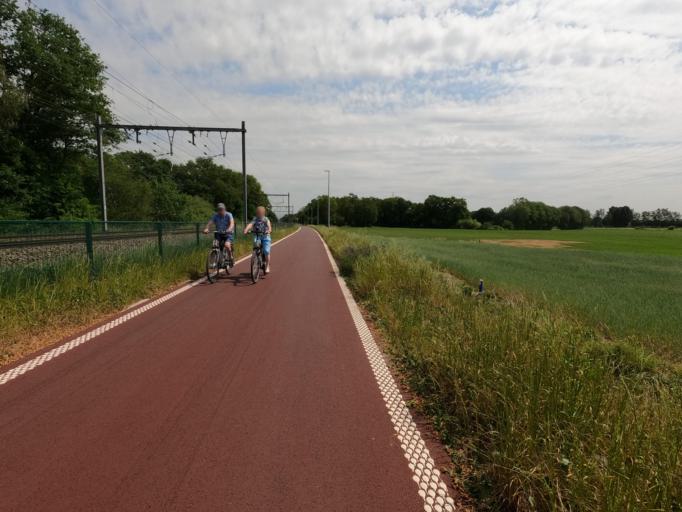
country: BE
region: Flanders
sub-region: Provincie Antwerpen
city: Olen
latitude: 51.1766
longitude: 4.8752
